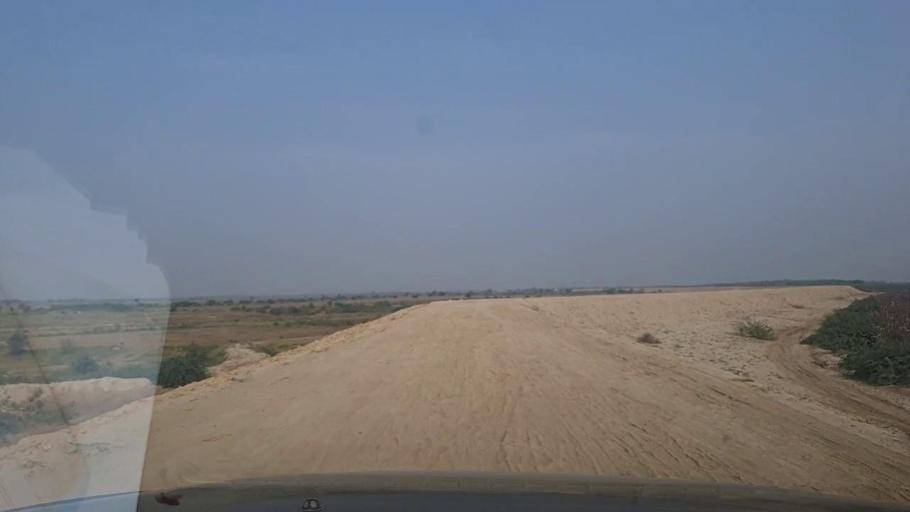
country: PK
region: Sindh
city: Bulri
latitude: 24.9568
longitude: 68.2910
